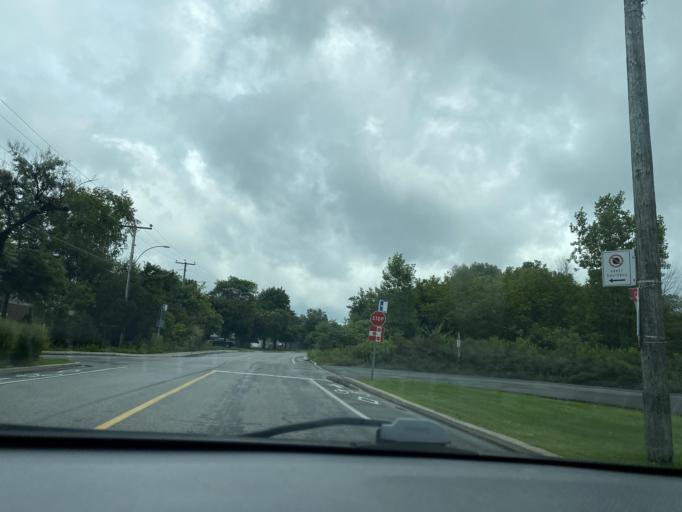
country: CA
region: Quebec
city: Baie-D'Urfe
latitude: 45.4376
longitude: -73.9014
